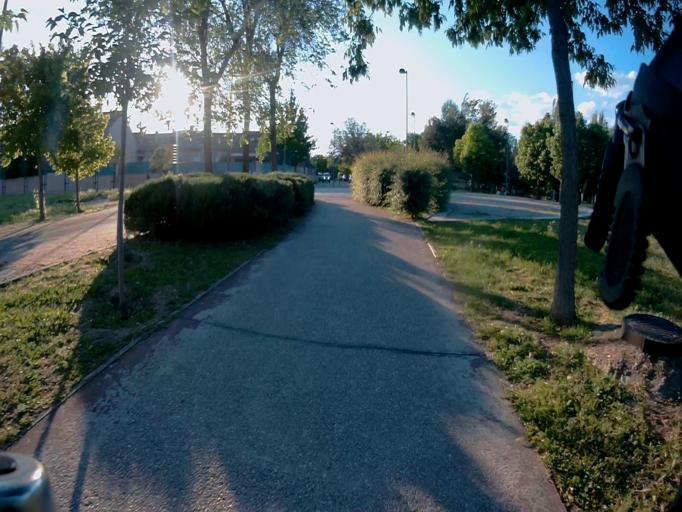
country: ES
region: Madrid
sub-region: Provincia de Madrid
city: Fuenlabrada
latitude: 40.3130
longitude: -3.7914
